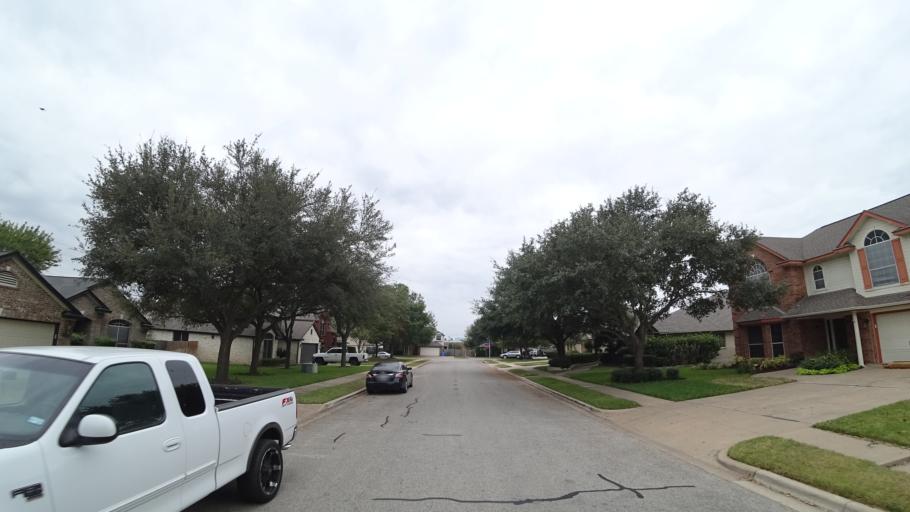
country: US
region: Texas
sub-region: Travis County
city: Pflugerville
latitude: 30.4544
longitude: -97.6176
